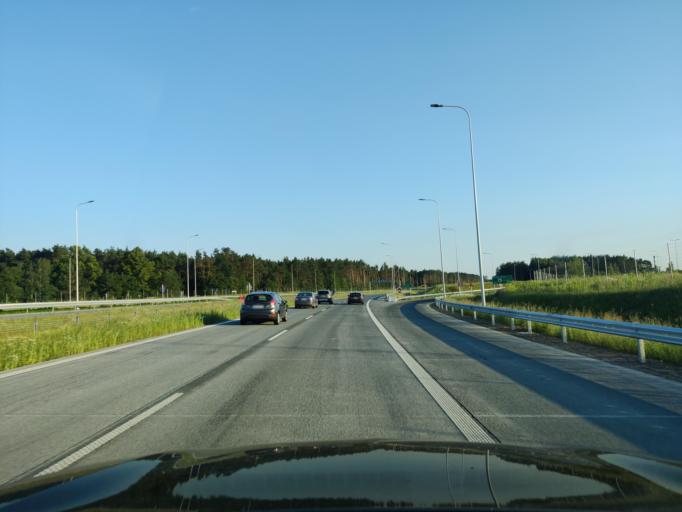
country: PL
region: Masovian Voivodeship
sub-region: Powiat mlawski
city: Strzegowo
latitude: 52.8596
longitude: 20.2872
